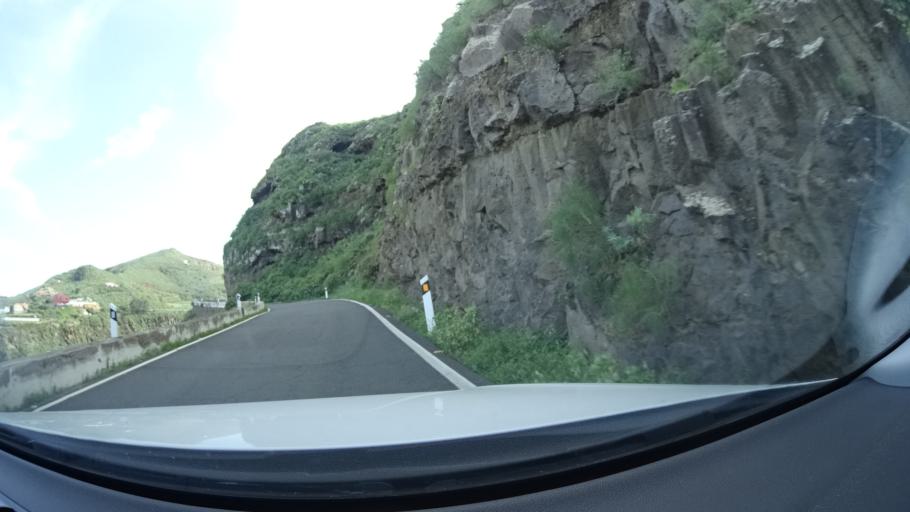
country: ES
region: Canary Islands
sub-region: Provincia de Las Palmas
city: Guia
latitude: 28.1149
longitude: -15.6419
